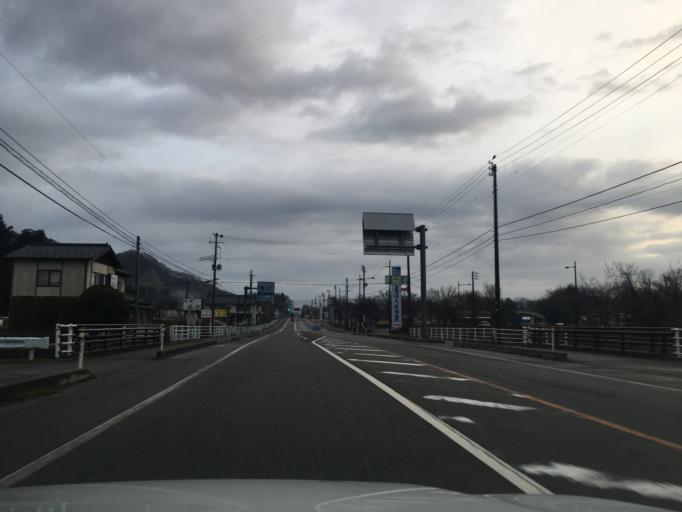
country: JP
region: Niigata
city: Murakami
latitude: 38.2810
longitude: 139.5209
